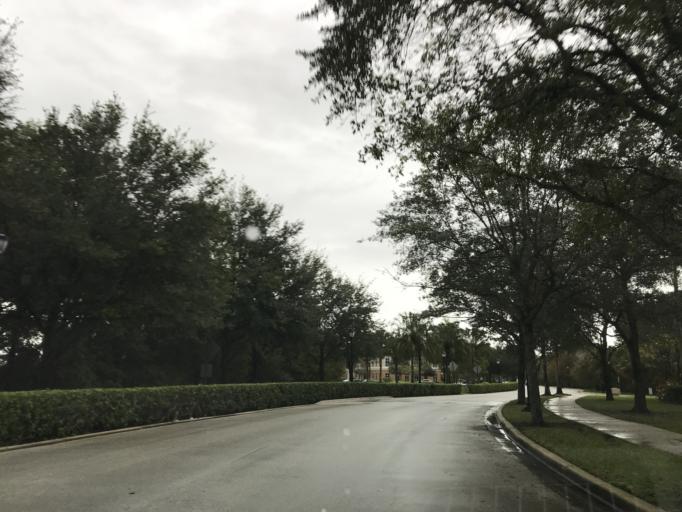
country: US
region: Florida
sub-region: Broward County
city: Coral Springs
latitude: 26.3066
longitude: -80.2835
